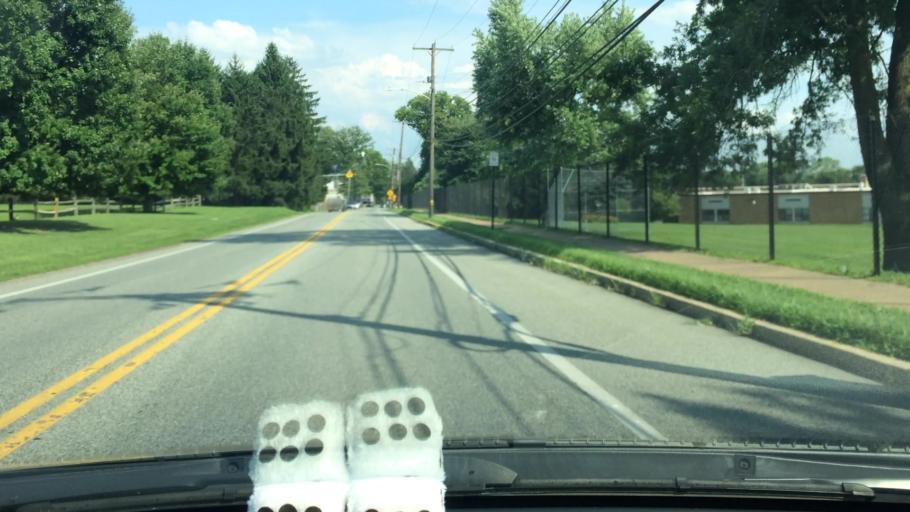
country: US
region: Pennsylvania
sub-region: Delaware County
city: Village Green-Green Ridge
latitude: 39.8721
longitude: -75.4432
